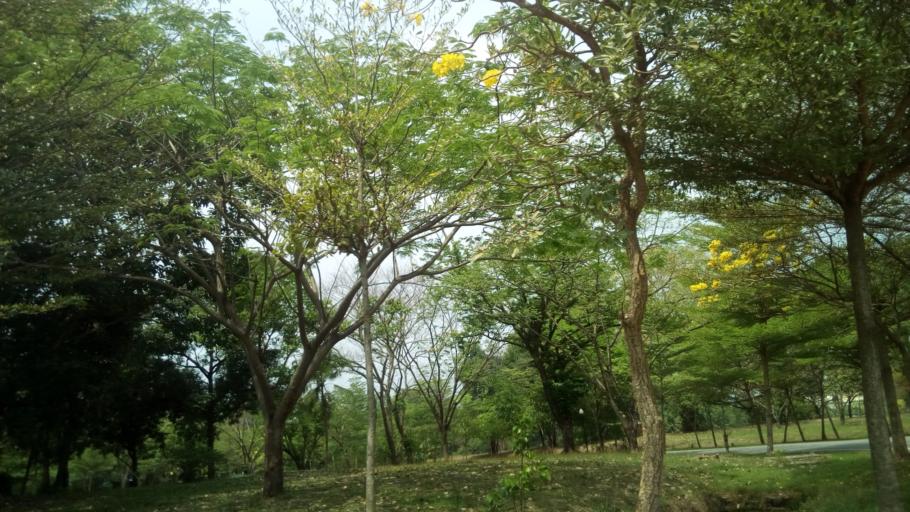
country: TH
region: Bangkok
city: Thawi Watthana
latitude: 13.7816
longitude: 100.3217
